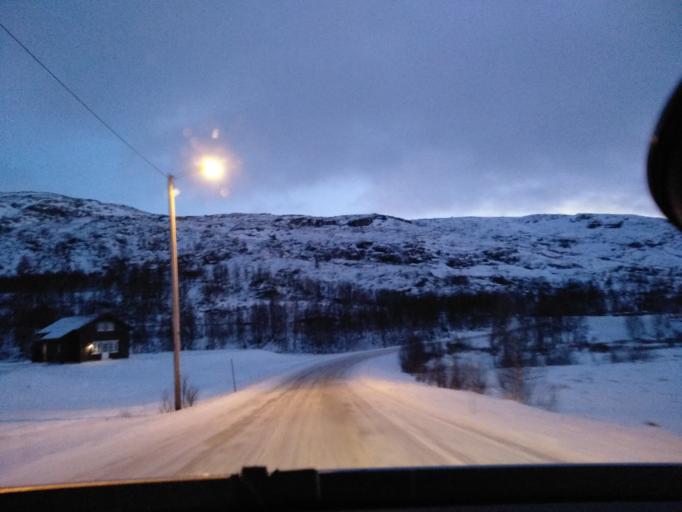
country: NO
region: Vest-Agder
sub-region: Sirdal
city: Tonstad
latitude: 59.0139
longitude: 6.9388
